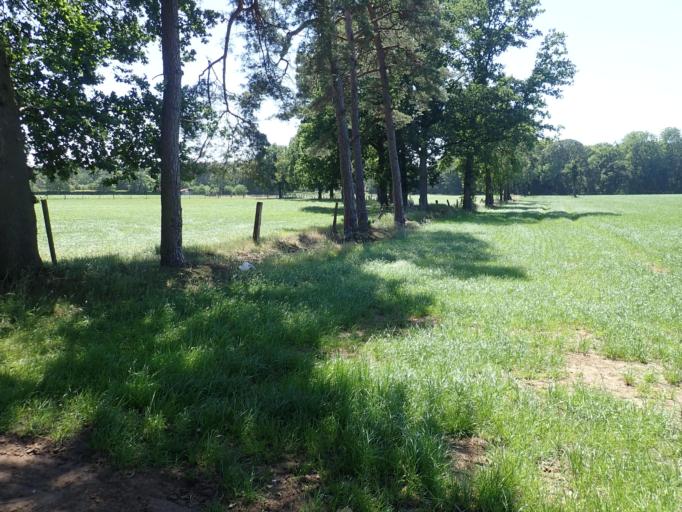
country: BE
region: Flanders
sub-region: Provincie Antwerpen
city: Beerse
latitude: 51.2863
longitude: 4.8337
